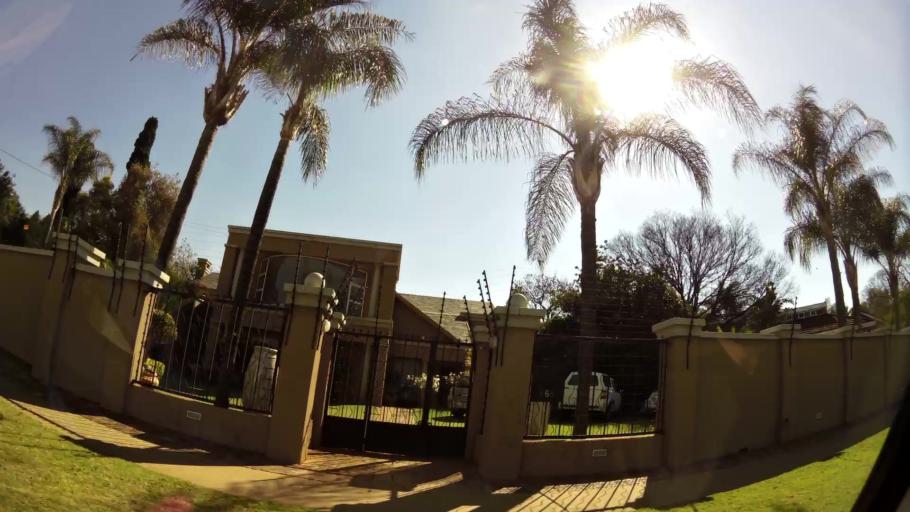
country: ZA
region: Gauteng
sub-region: City of Tshwane Metropolitan Municipality
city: Pretoria
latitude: -25.7595
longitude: 28.2719
